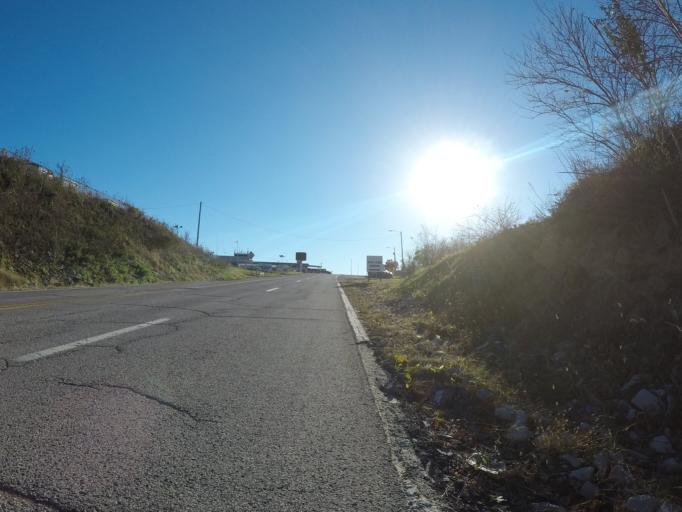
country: US
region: West Virginia
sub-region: Wayne County
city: Ceredo
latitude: 38.3711
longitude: -82.5549
